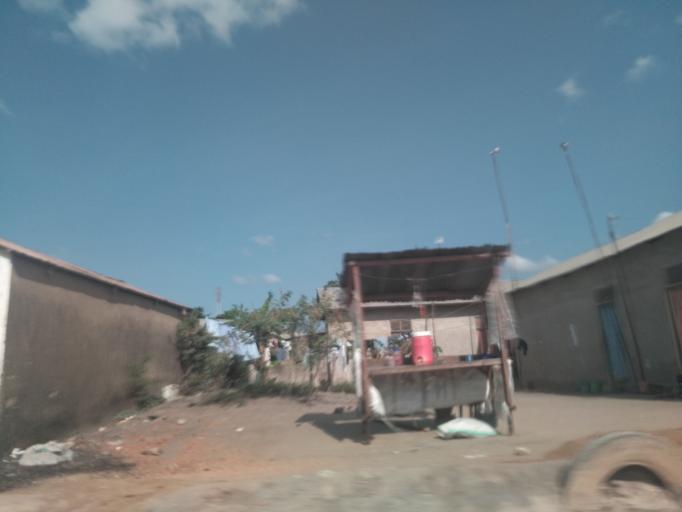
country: TZ
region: Dar es Salaam
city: Dar es Salaam
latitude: -6.9105
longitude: 39.2869
